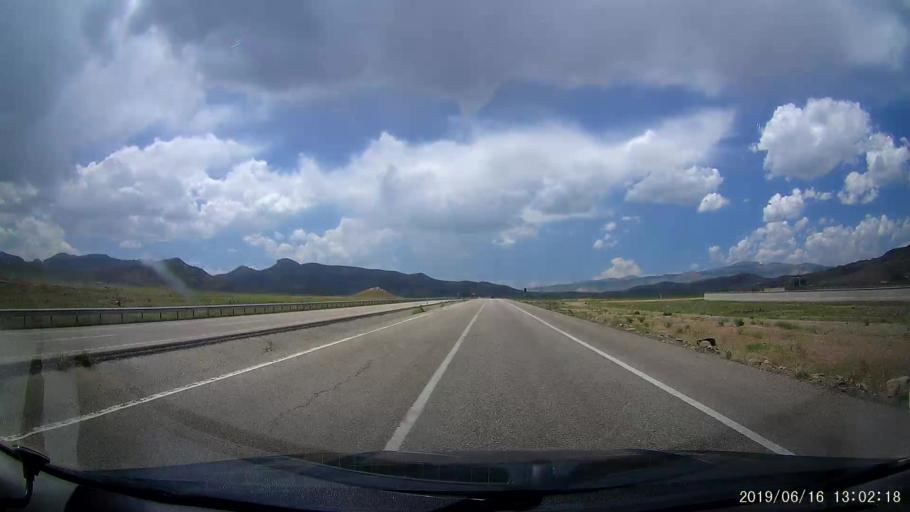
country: TR
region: Agri
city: Sulucem
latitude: 39.5739
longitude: 43.8199
